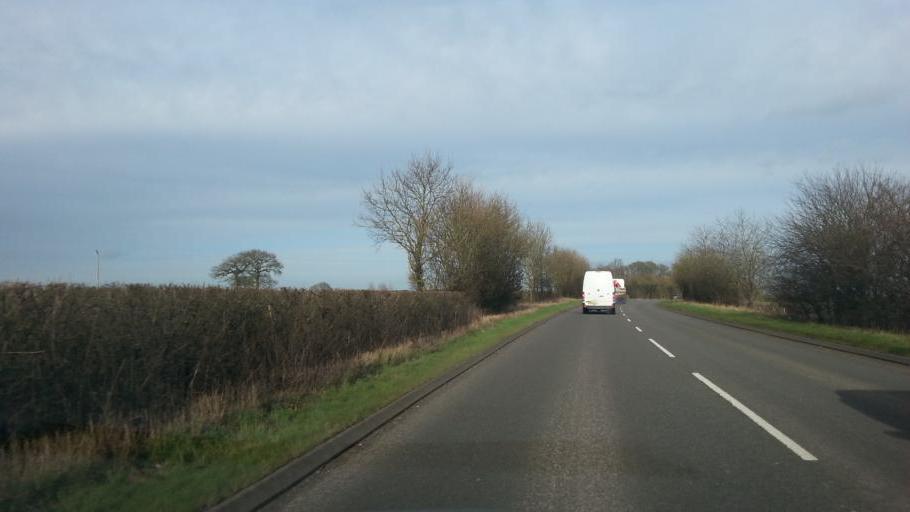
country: GB
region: England
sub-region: Staffordshire
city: Colwich
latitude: 52.8632
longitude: -1.9529
